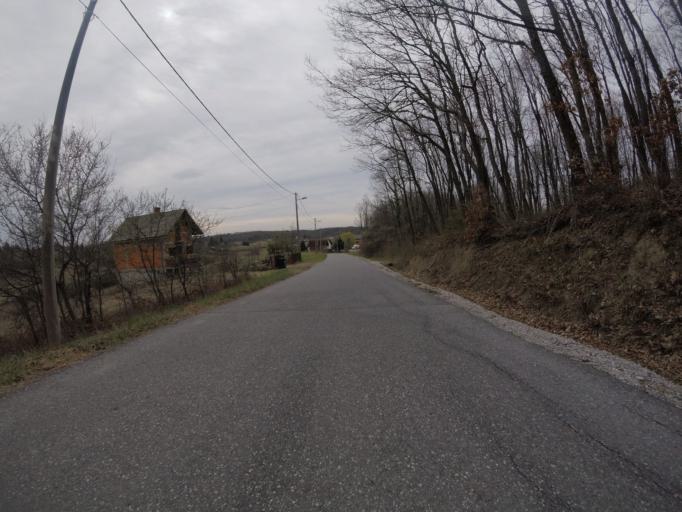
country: HR
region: Grad Zagreb
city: Strmec
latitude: 45.6296
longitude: 15.9350
